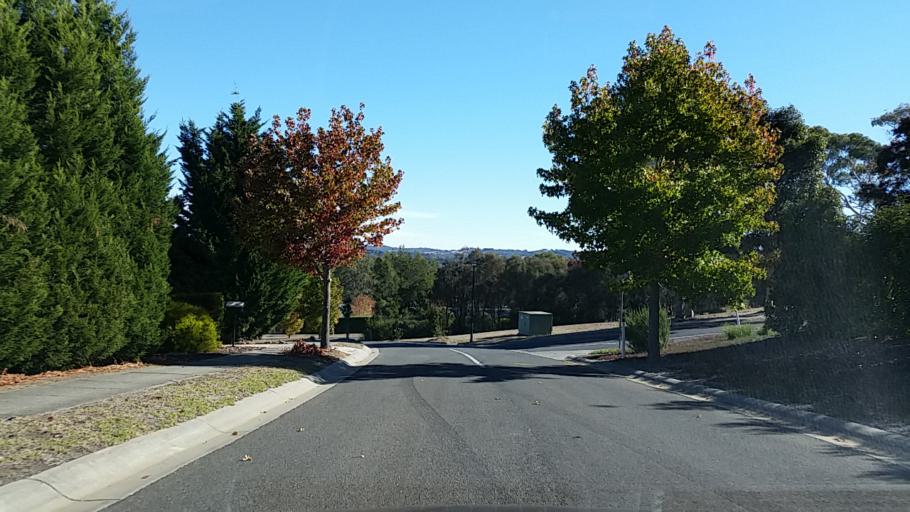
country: AU
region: South Australia
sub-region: Mount Barker
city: Mount Barker
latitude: -35.0615
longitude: 138.8815
